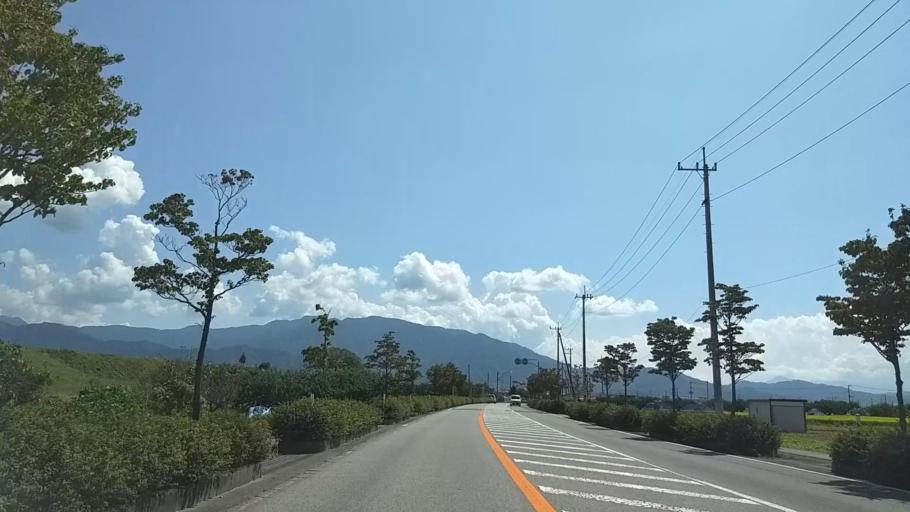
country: JP
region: Yamanashi
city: Ryuo
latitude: 35.6065
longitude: 138.5049
